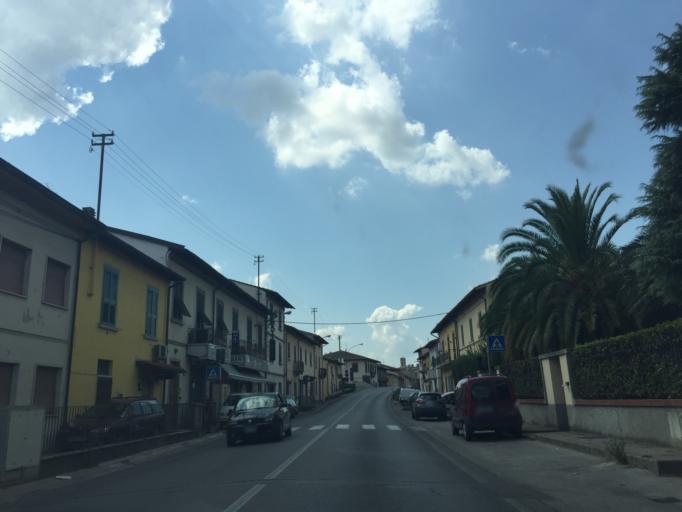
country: IT
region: Tuscany
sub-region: Provincia di Prato
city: Poggio A Caiano
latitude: 43.8141
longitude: 11.0633
